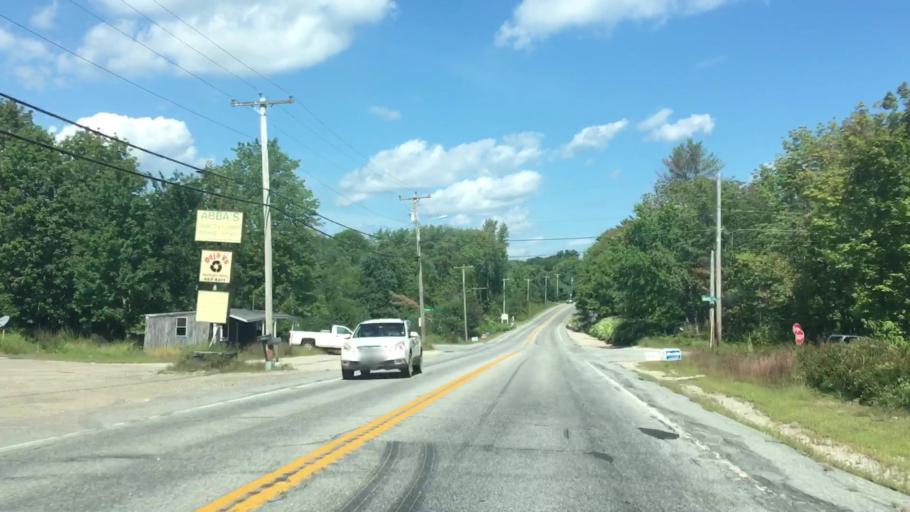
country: US
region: Maine
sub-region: Cumberland County
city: New Gloucester
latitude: 43.9169
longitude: -70.3179
